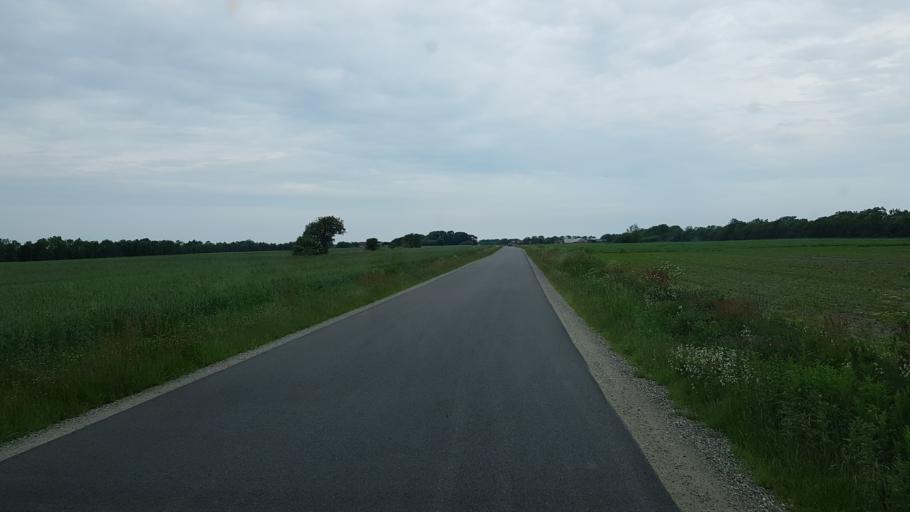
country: DK
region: South Denmark
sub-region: Varde Kommune
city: Oksbol
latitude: 55.7168
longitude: 8.3679
